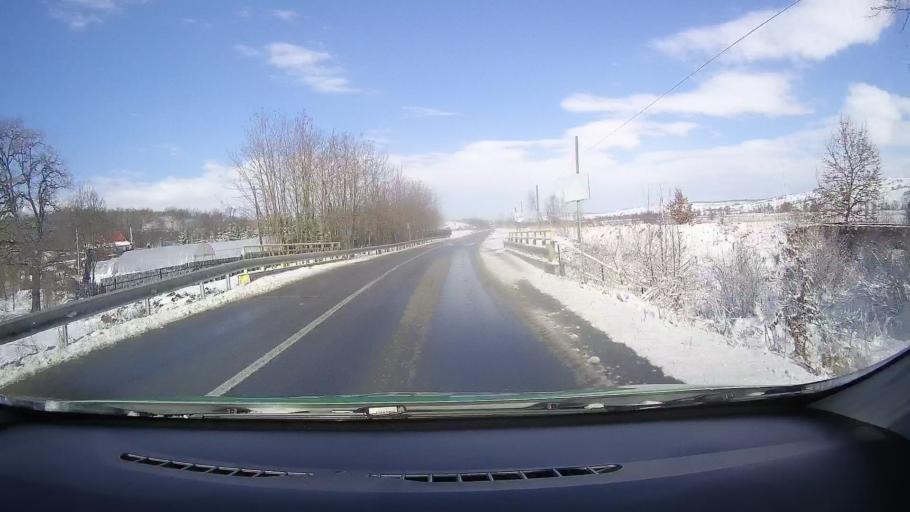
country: RO
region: Sibiu
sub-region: Comuna Nocrich
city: Nocrich
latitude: 45.8712
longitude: 24.4511
